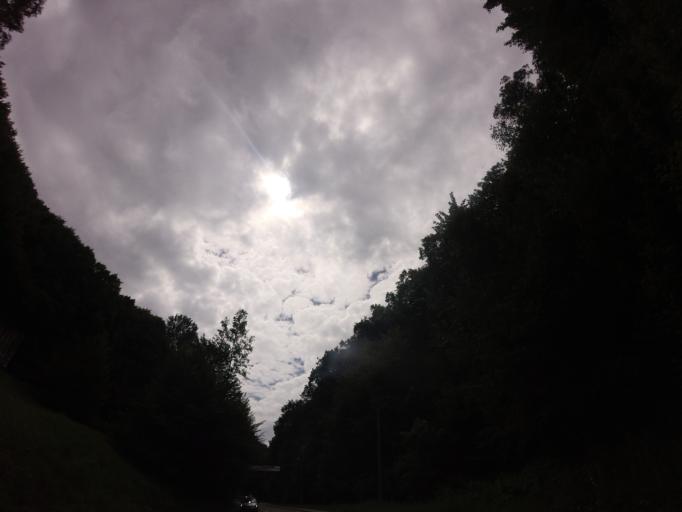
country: PL
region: Lublin Voivodeship
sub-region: Powiat pulawski
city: Kazimierz Dolny
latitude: 51.3138
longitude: 21.9524
